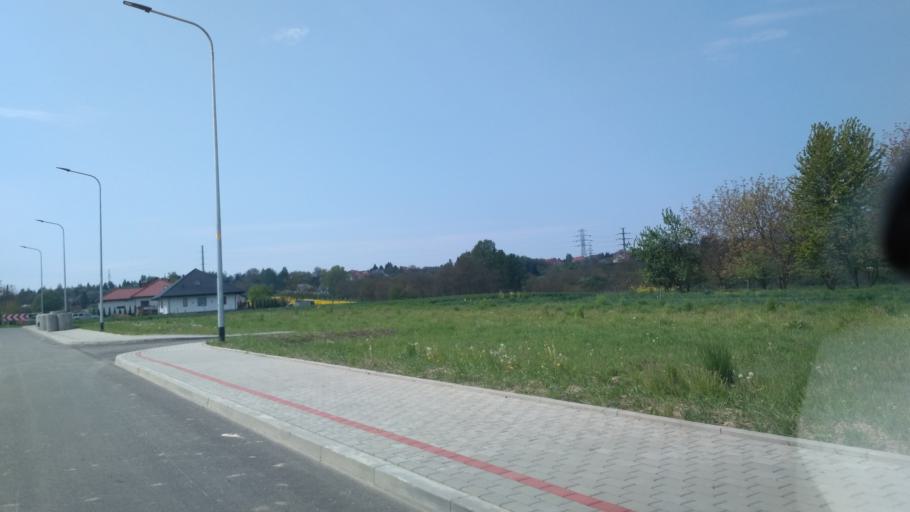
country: PL
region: Subcarpathian Voivodeship
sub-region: Powiat jaroslawski
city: Jaroslaw
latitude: 50.0022
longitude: 22.6806
